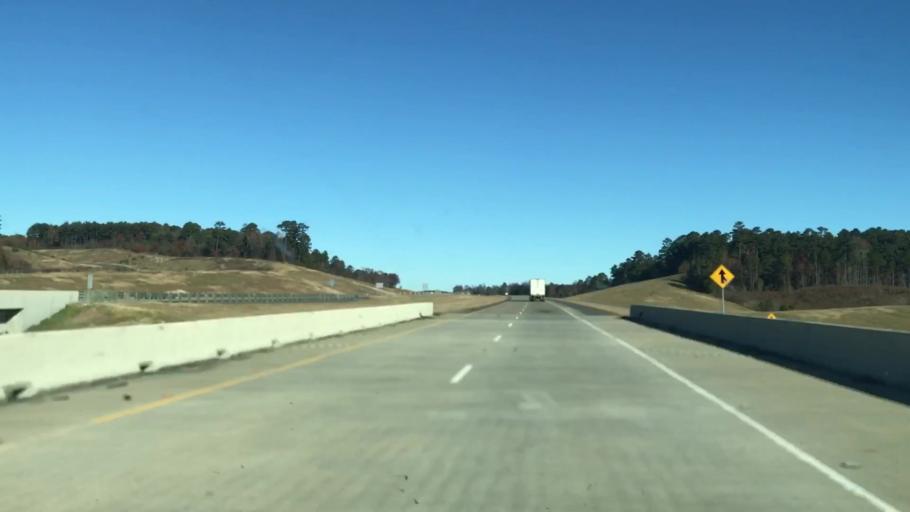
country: US
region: Louisiana
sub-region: Caddo Parish
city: Vivian
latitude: 32.9436
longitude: -93.8976
